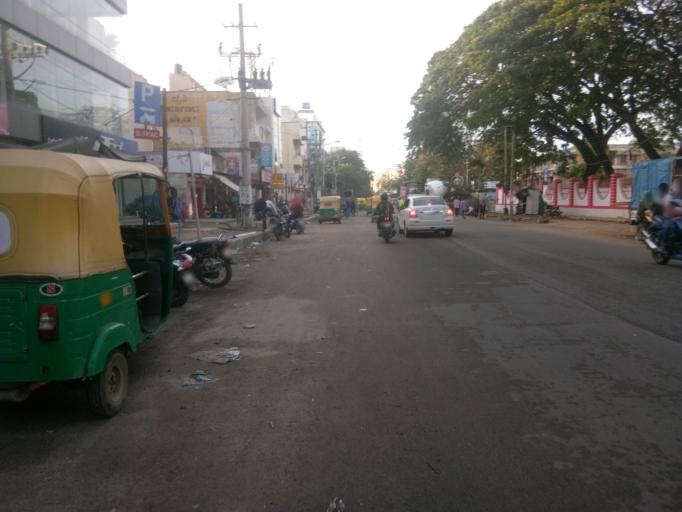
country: IN
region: Karnataka
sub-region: Bangalore Urban
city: Bangalore
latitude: 13.0173
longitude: 77.6359
